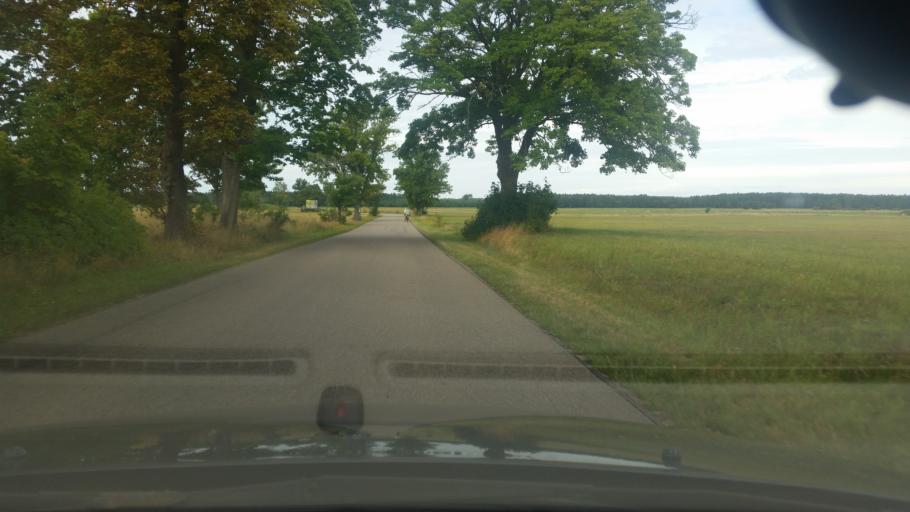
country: PL
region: Pomeranian Voivodeship
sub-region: Powiat leborski
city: Leba
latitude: 54.7298
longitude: 17.6089
